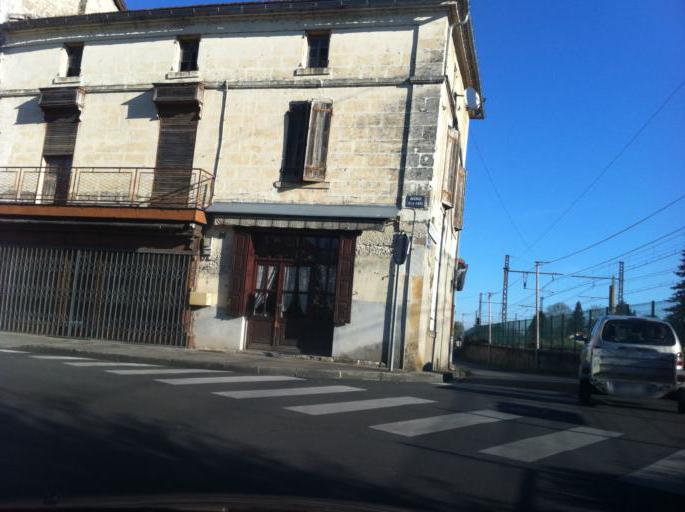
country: FR
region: Aquitaine
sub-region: Departement de la Dordogne
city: Saint-Aulaye
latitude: 45.2673
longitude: 0.1683
